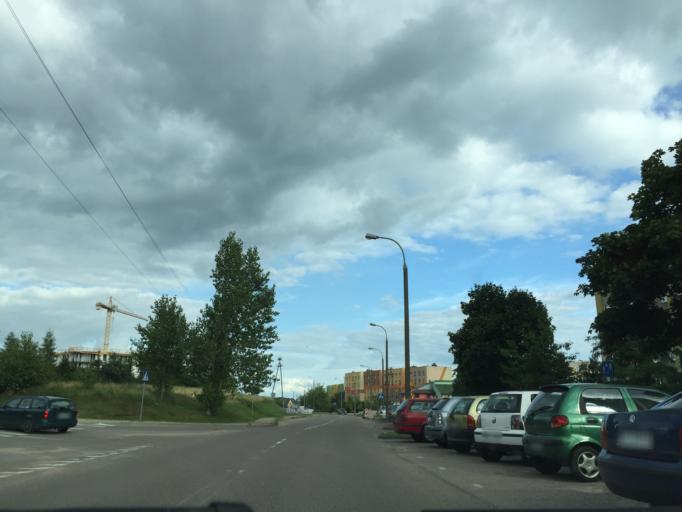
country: PL
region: Podlasie
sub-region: Suwalki
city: Suwalki
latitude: 54.1231
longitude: 22.9450
